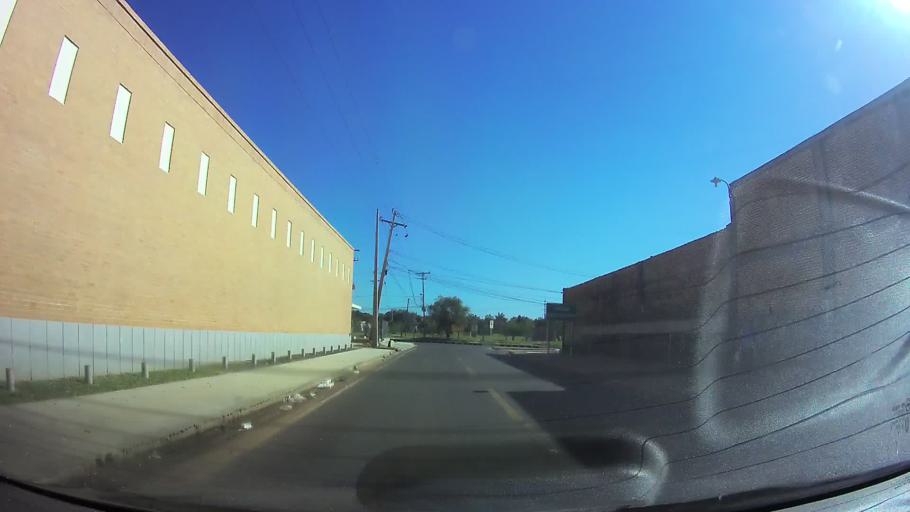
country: PY
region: Central
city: Fernando de la Mora
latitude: -25.2907
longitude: -57.5425
